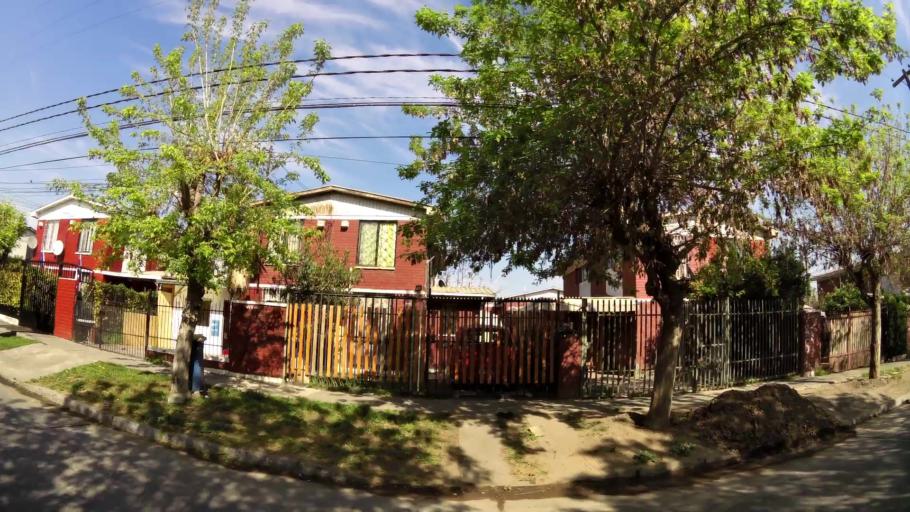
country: CL
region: Santiago Metropolitan
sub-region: Provincia de Santiago
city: La Pintana
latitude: -33.5549
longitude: -70.6001
